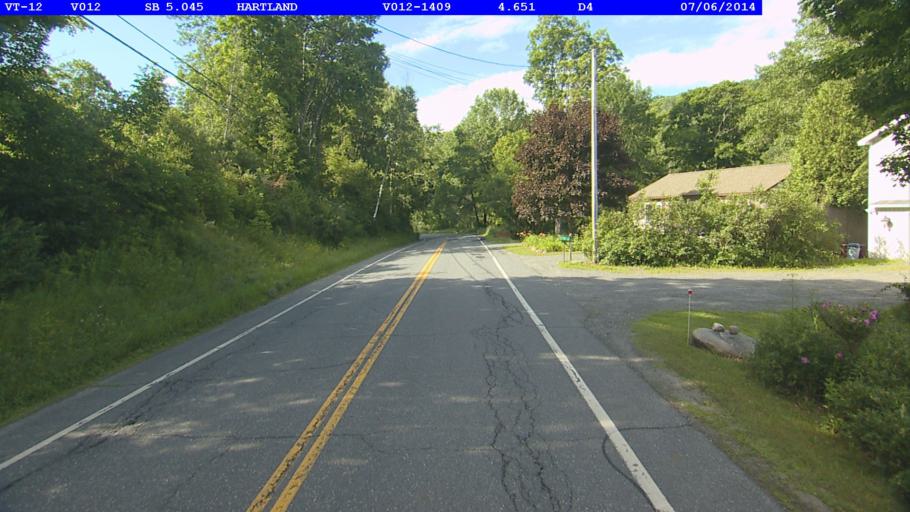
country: US
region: Vermont
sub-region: Windsor County
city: Woodstock
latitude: 43.5847
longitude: -72.4492
